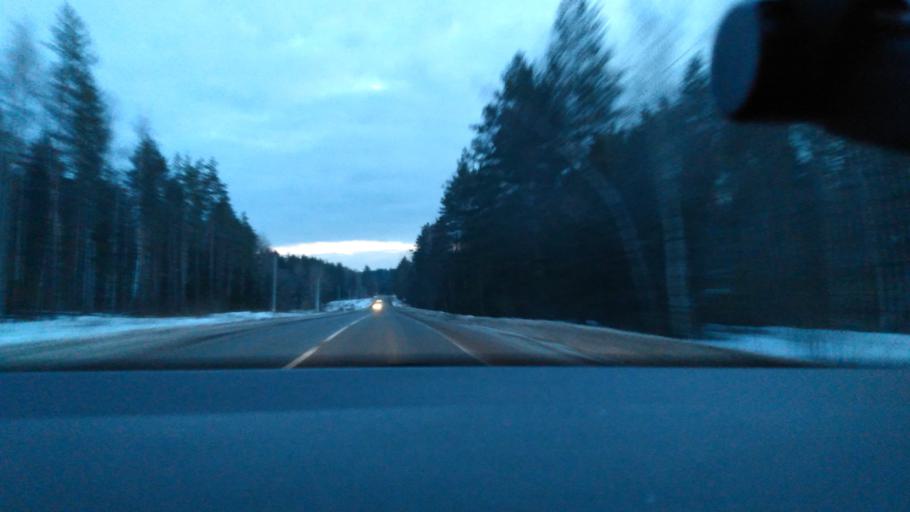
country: RU
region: Moskovskaya
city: Yegor'yevsk
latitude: 55.3222
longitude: 39.0728
